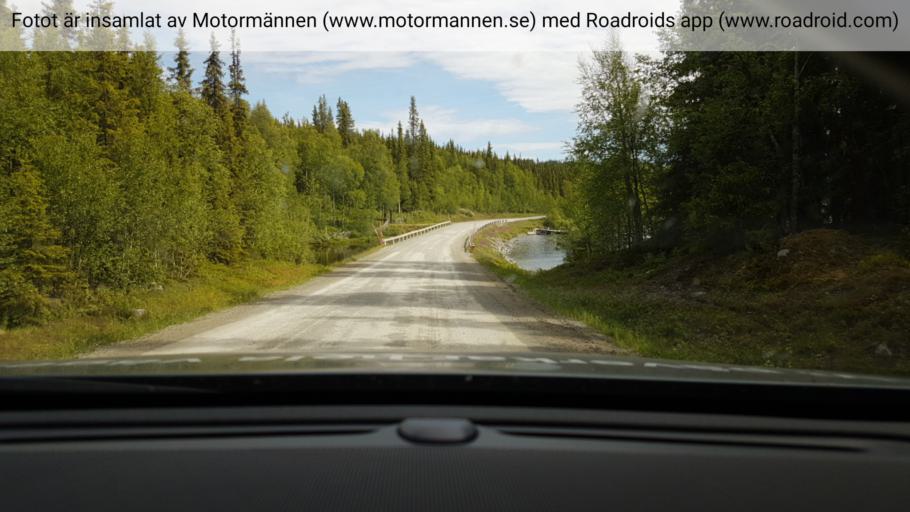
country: SE
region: Vaesterbotten
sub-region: Vilhelmina Kommun
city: Sjoberg
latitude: 65.2111
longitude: 16.0729
